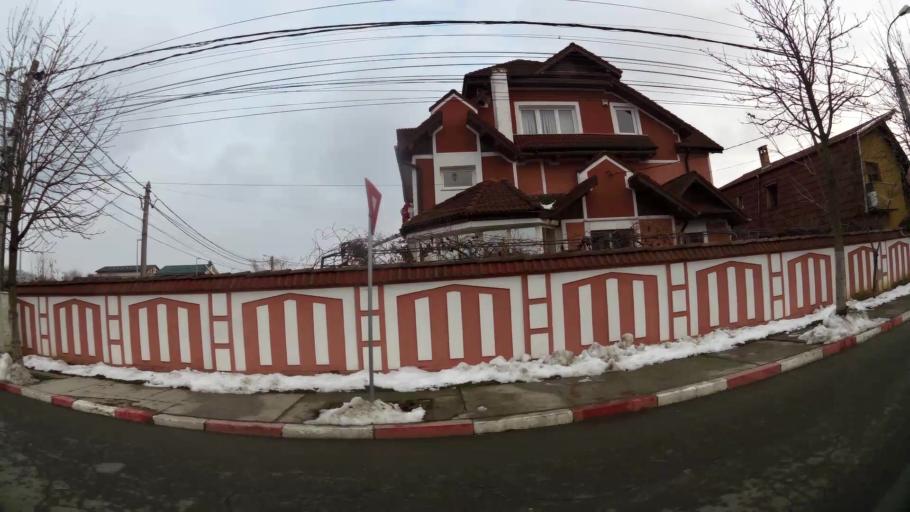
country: RO
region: Ilfov
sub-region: Voluntari City
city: Voluntari
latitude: 44.4985
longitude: 26.1699
